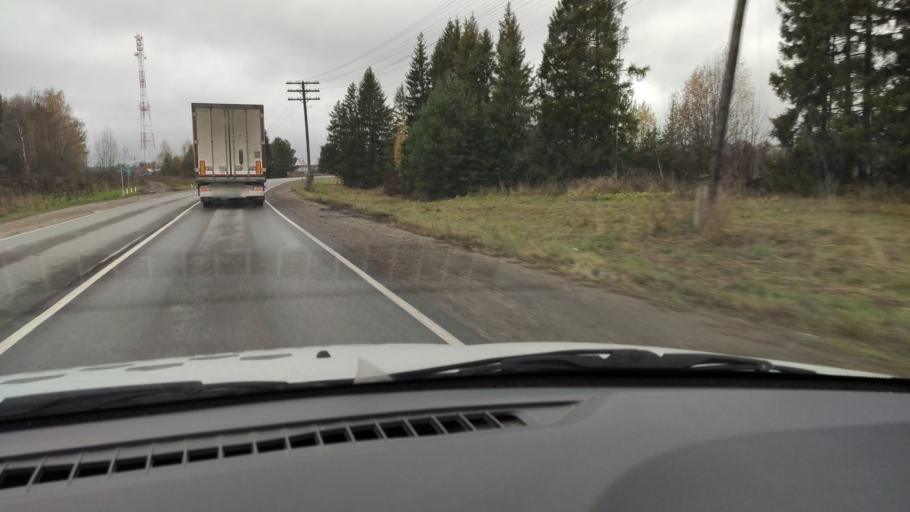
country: RU
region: Kirov
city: Slobodskoy
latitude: 58.7801
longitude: 50.4436
